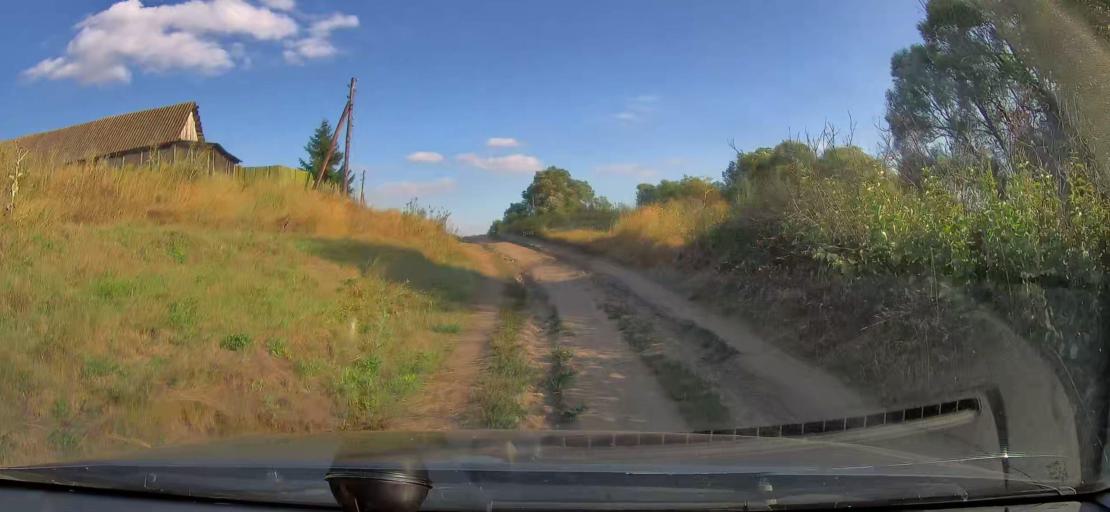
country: RU
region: Kursk
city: Zolotukhino
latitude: 52.0285
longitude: 36.2011
